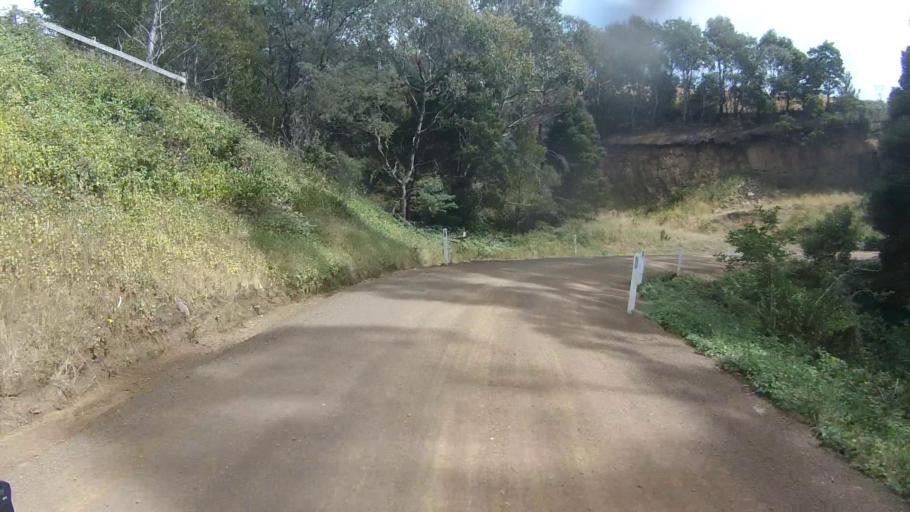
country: AU
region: Tasmania
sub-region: Sorell
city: Sorell
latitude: -42.7870
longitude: 147.8414
